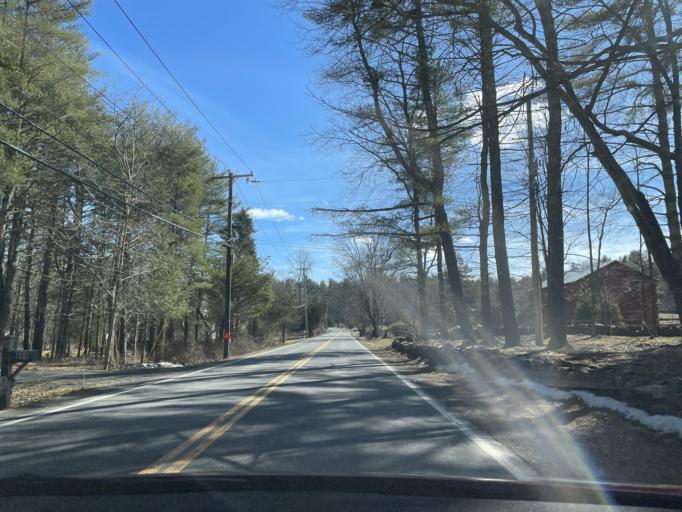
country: US
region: New York
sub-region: Ulster County
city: Zena
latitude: 42.0264
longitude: -74.0823
